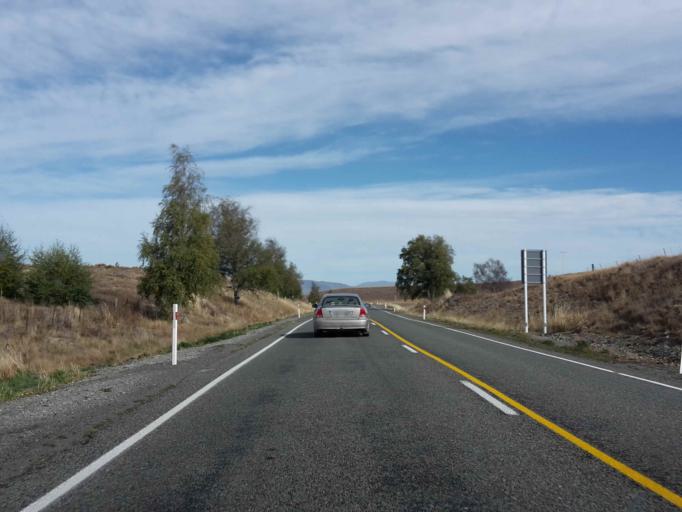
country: NZ
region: Canterbury
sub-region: Timaru District
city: Pleasant Point
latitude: -44.0158
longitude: 170.5011
